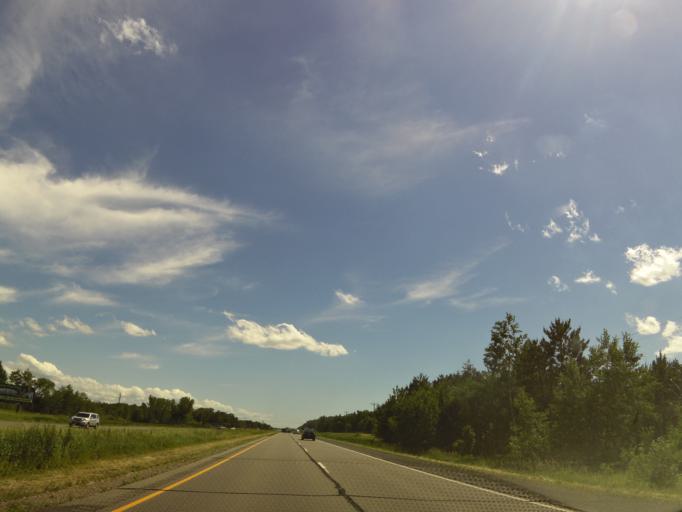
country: US
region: Minnesota
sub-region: Stearns County
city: Sartell
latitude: 45.6816
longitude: -94.1736
